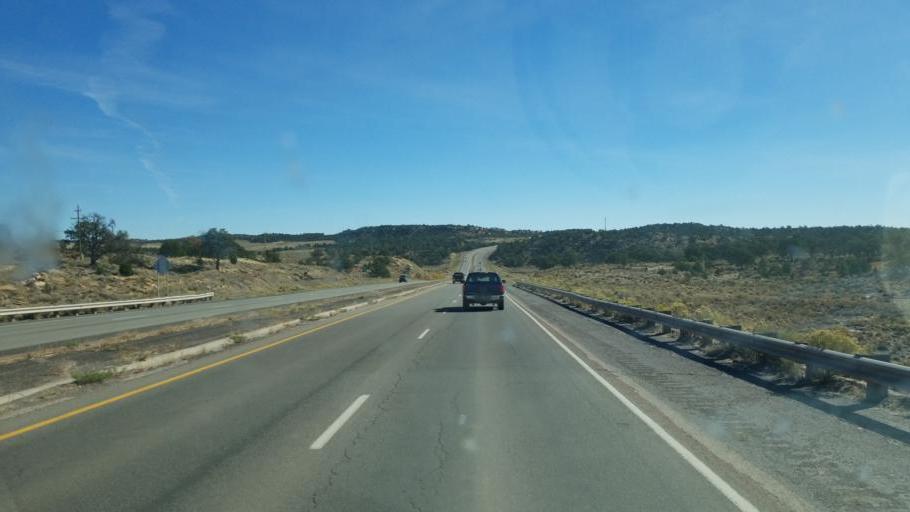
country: US
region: Arizona
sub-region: Apache County
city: Window Rock
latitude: 35.6370
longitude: -108.9830
